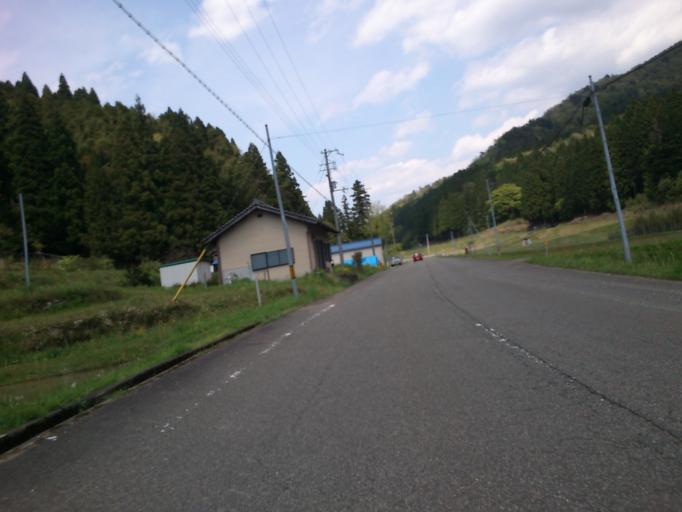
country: JP
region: Kyoto
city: Fukuchiyama
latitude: 35.3794
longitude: 134.9386
